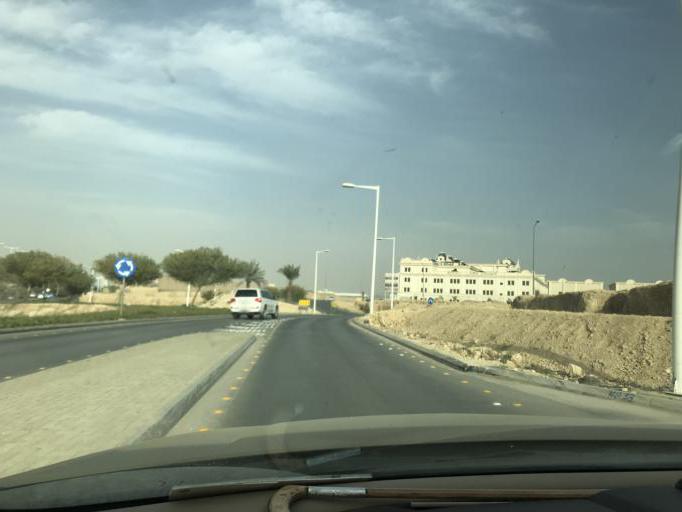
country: SA
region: Ar Riyad
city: Riyadh
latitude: 24.7346
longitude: 46.7406
